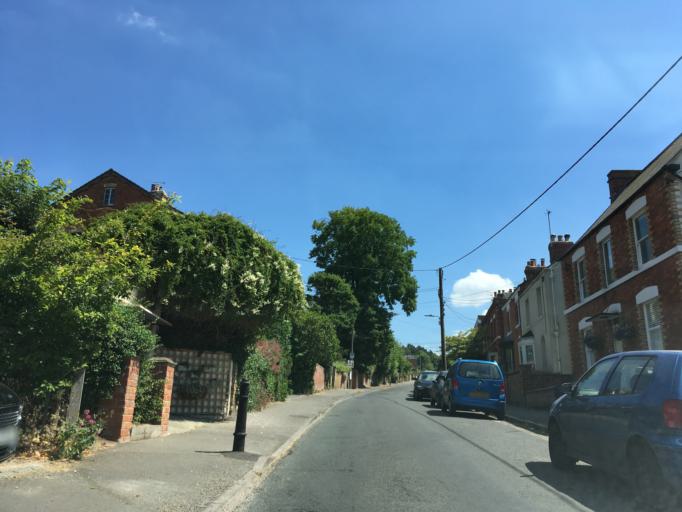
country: GB
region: England
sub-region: Gloucestershire
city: Stroud
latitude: 51.7435
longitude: -2.2050
